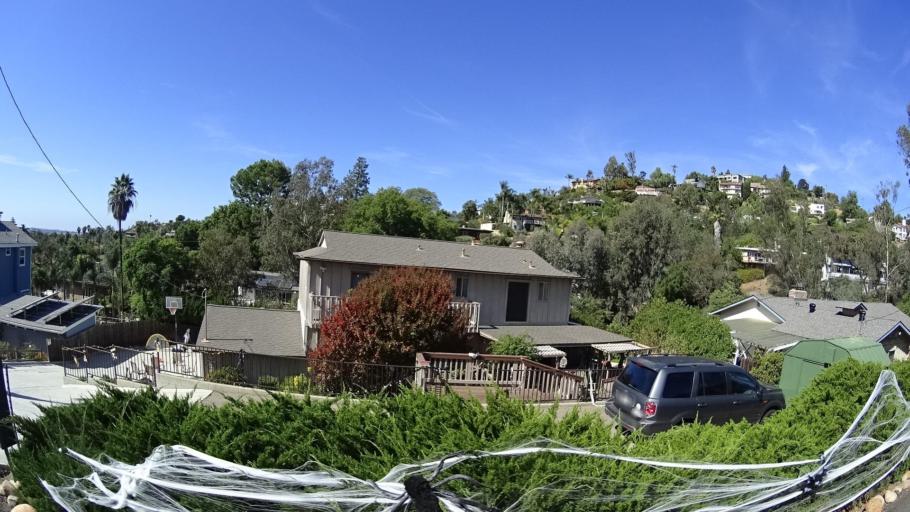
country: US
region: California
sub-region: San Diego County
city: Casa de Oro-Mount Helix
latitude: 32.7575
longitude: -116.9658
